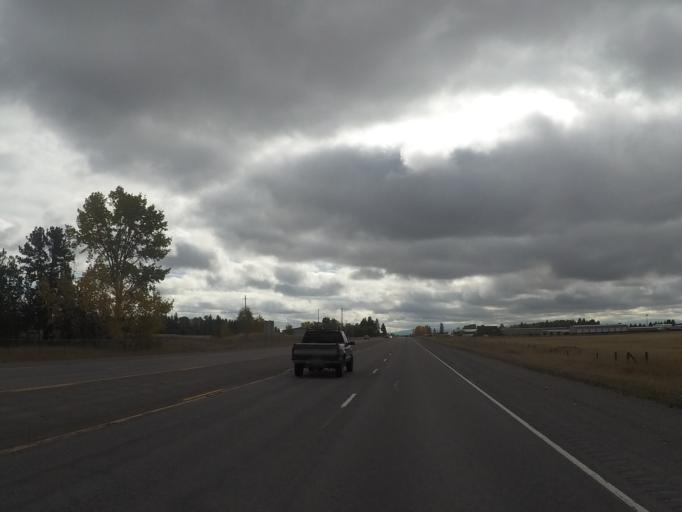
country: US
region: Montana
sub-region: Flathead County
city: Columbia Falls
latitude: 48.3666
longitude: -114.2411
